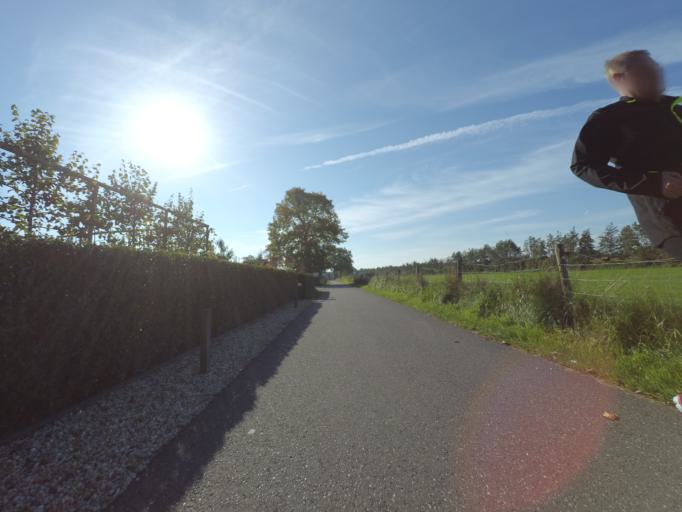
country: NL
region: Gelderland
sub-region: Gemeente Nijkerk
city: Nijkerk
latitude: 52.1854
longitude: 5.4616
